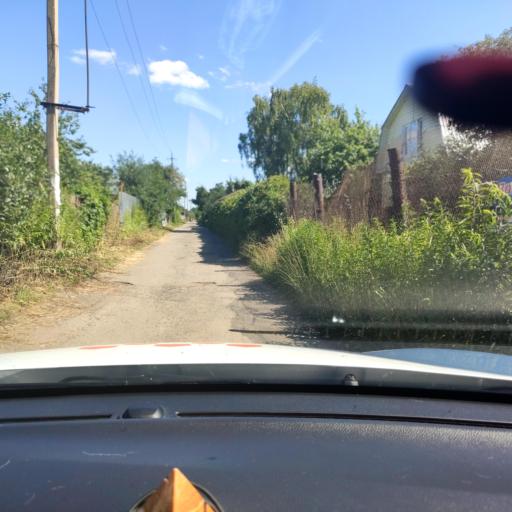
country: RU
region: Tatarstan
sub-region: Zelenodol'skiy Rayon
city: Vasil'yevo
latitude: 55.8264
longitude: 48.7449
